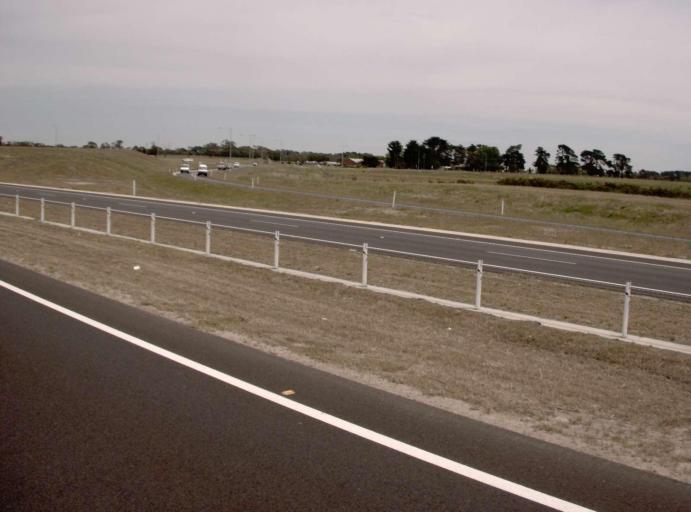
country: AU
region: Victoria
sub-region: Mornington Peninsula
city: Moorooduc
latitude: -38.2490
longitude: 145.1196
